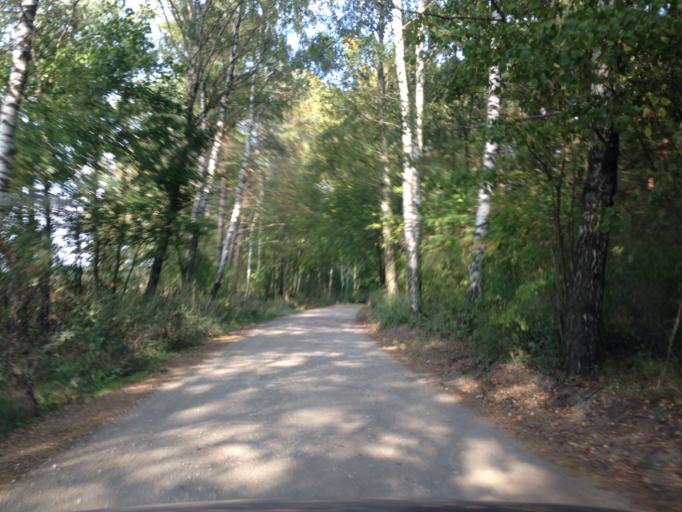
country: PL
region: Kujawsko-Pomorskie
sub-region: Powiat brodnicki
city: Gorzno
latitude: 53.2173
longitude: 19.6403
